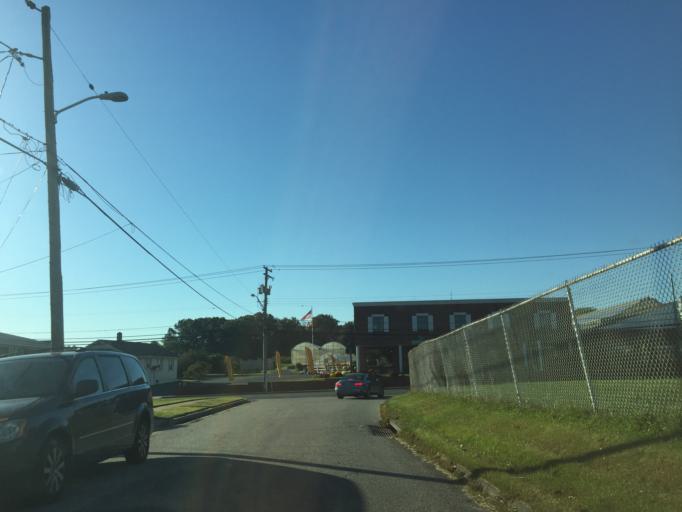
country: US
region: Maryland
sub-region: Baltimore County
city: Dundalk
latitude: 39.2834
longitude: -76.5179
